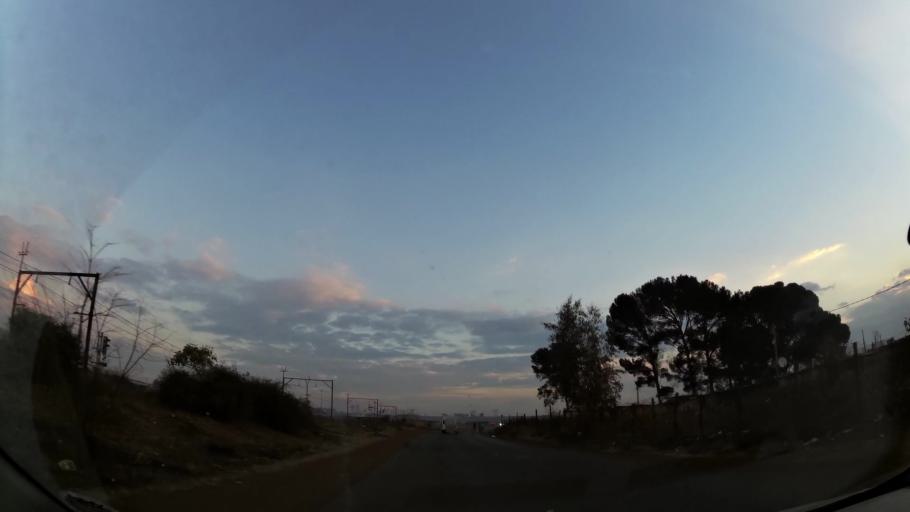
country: ZA
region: Gauteng
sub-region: City of Johannesburg Metropolitan Municipality
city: Orange Farm
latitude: -26.5544
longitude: 27.8804
